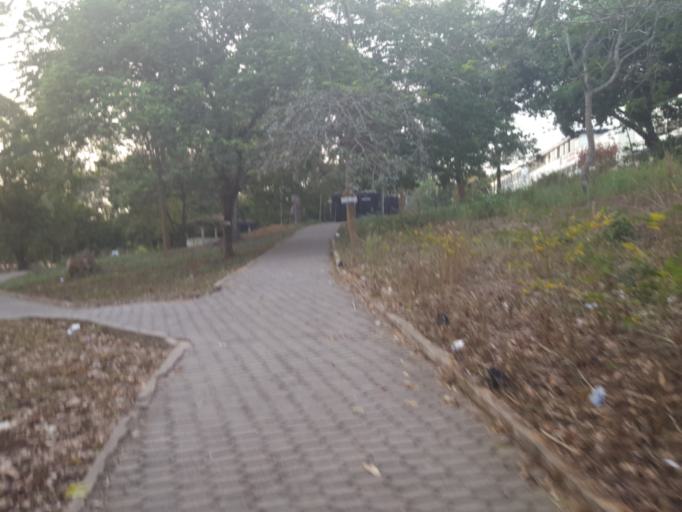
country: GH
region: Central
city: Cape Coast
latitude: 5.1156
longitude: -1.2832
